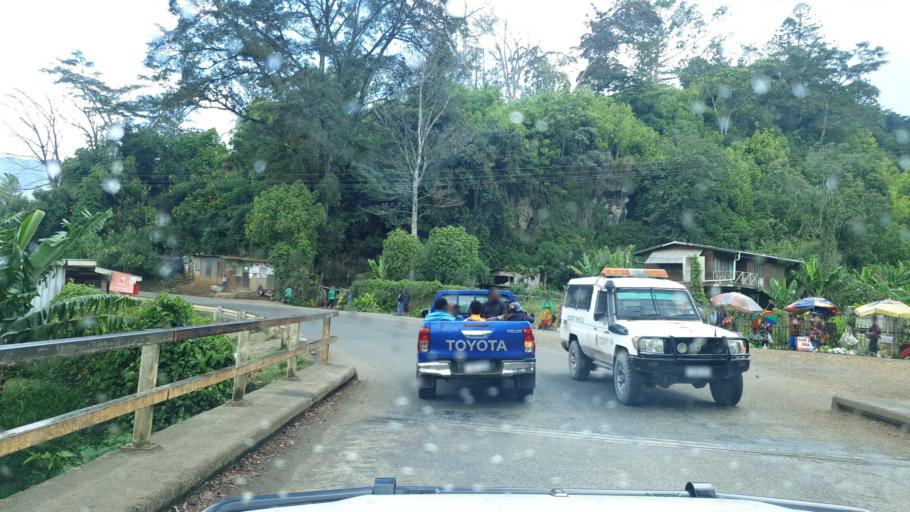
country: PG
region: Eastern Highlands
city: Goroka
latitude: -6.0086
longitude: 145.3093
